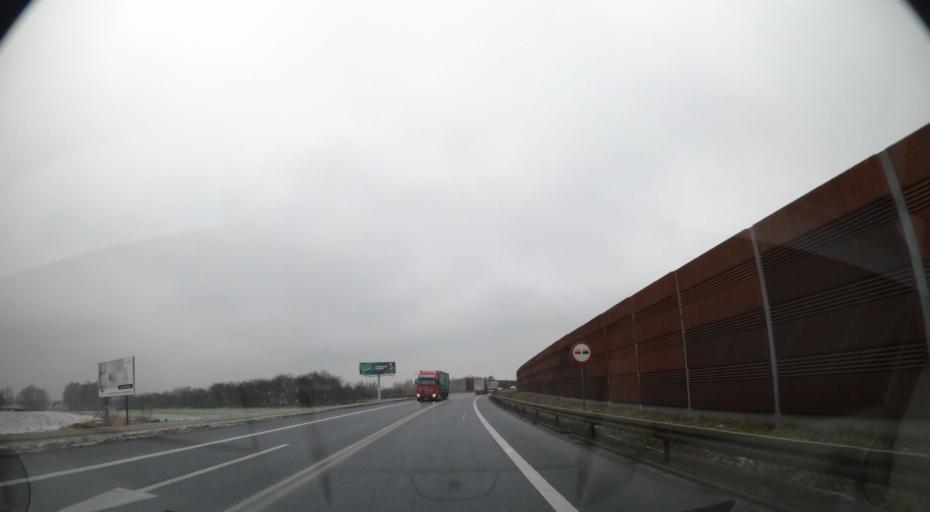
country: PL
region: Masovian Voivodeship
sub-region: Powiat sochaczewski
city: Sochaczew
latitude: 52.2061
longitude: 20.2360
